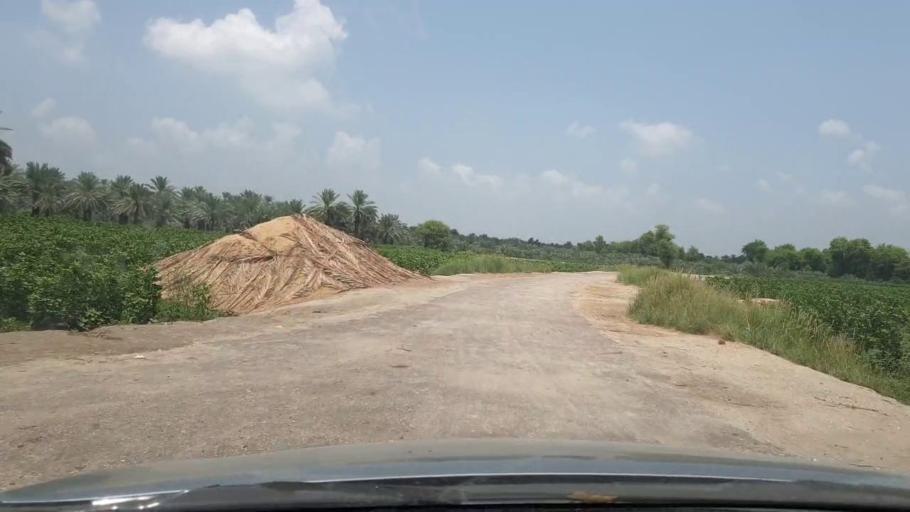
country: PK
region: Sindh
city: Khairpur
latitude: 27.4733
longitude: 68.7320
